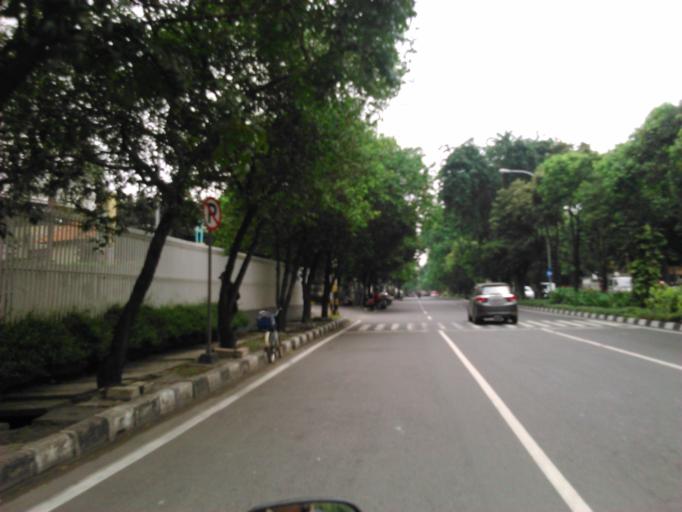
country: ID
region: East Java
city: Pacarkeling
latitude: -7.2617
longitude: 112.7512
